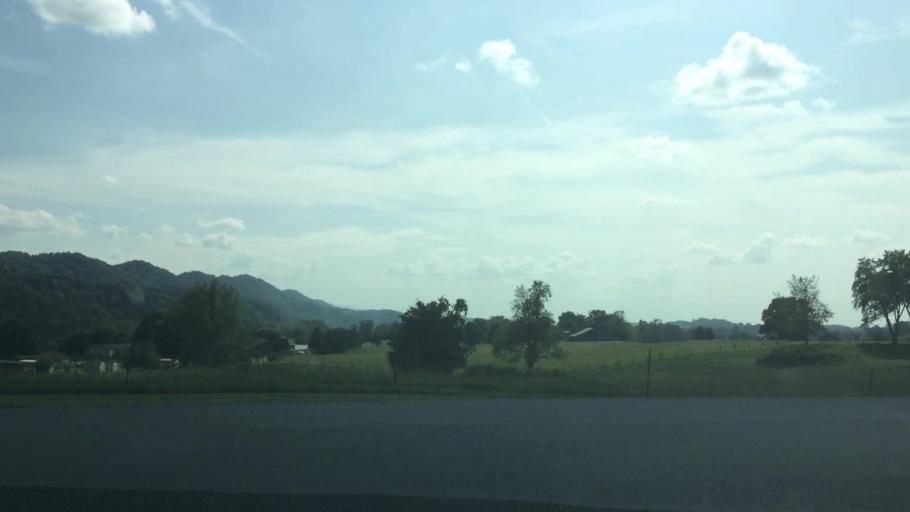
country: US
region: Tennessee
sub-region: Sullivan County
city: Fairmount
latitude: 36.5799
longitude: -82.0455
